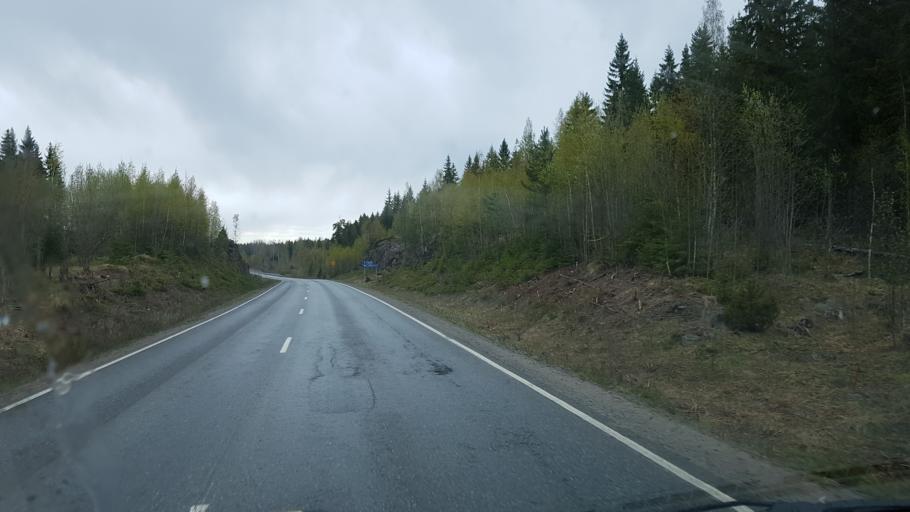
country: FI
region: Pirkanmaa
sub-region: Tampere
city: Pirkkala
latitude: 61.4058
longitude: 23.6329
